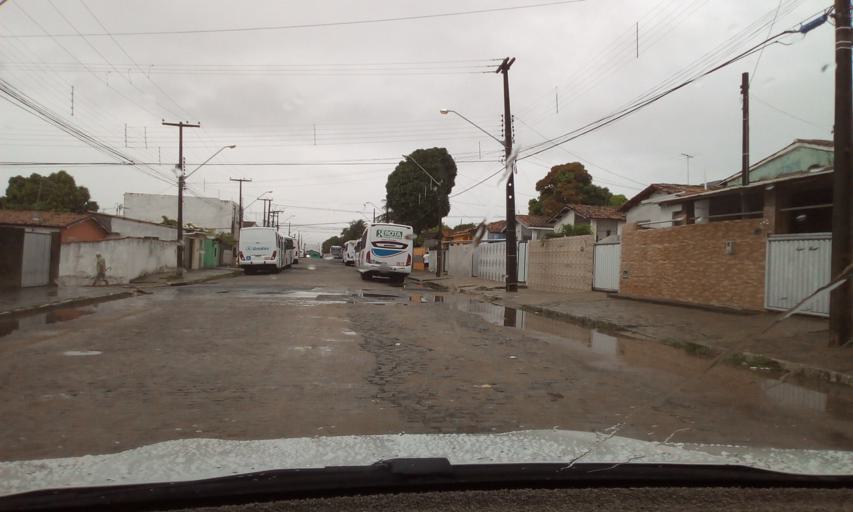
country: BR
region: Paraiba
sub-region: Joao Pessoa
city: Joao Pessoa
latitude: -7.1890
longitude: -34.8380
